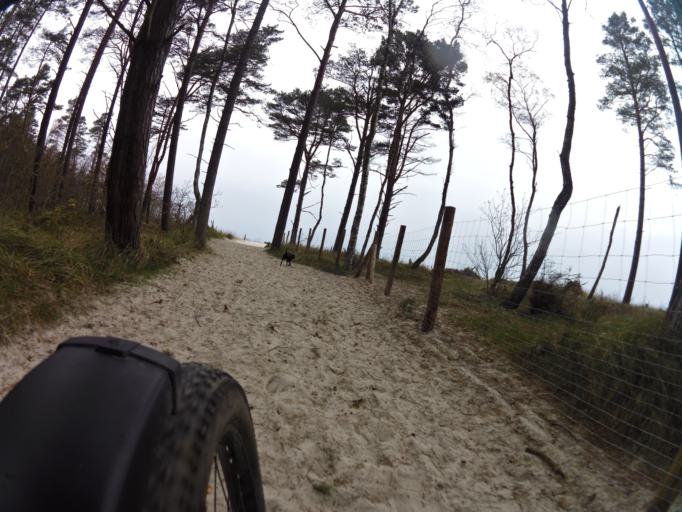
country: PL
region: Pomeranian Voivodeship
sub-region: Powiat pucki
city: Krokowa
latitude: 54.8314
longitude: 18.1240
